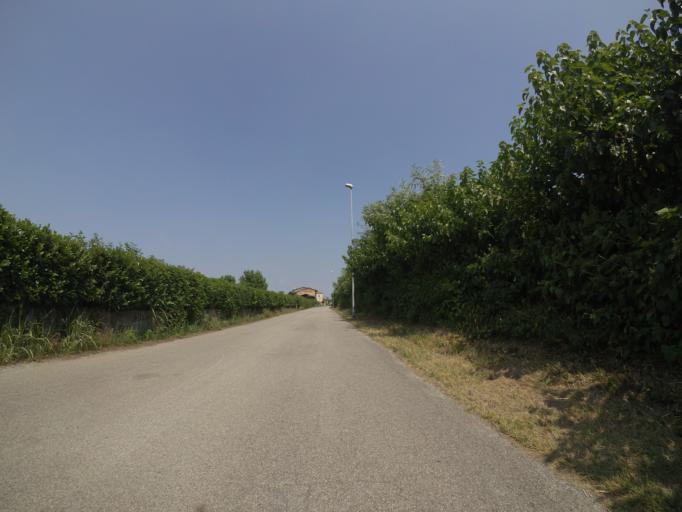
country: IT
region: Friuli Venezia Giulia
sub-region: Provincia di Udine
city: Basiliano-Vissandone
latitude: 46.0145
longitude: 13.1028
